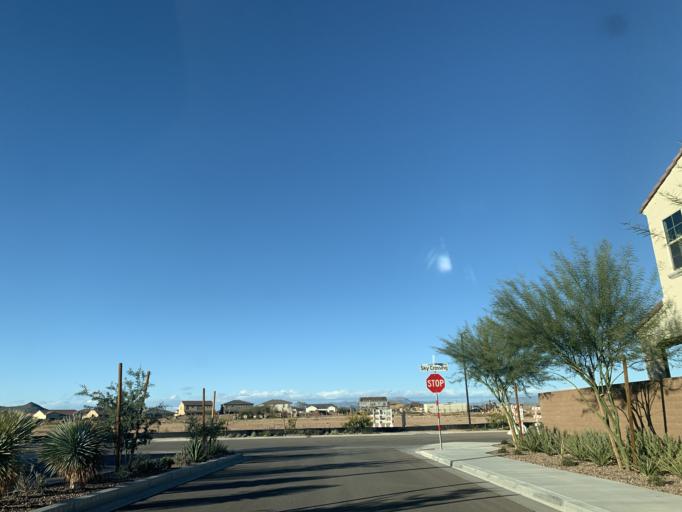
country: US
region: Arizona
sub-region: Maricopa County
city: Cave Creek
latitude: 33.6871
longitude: -112.0109
